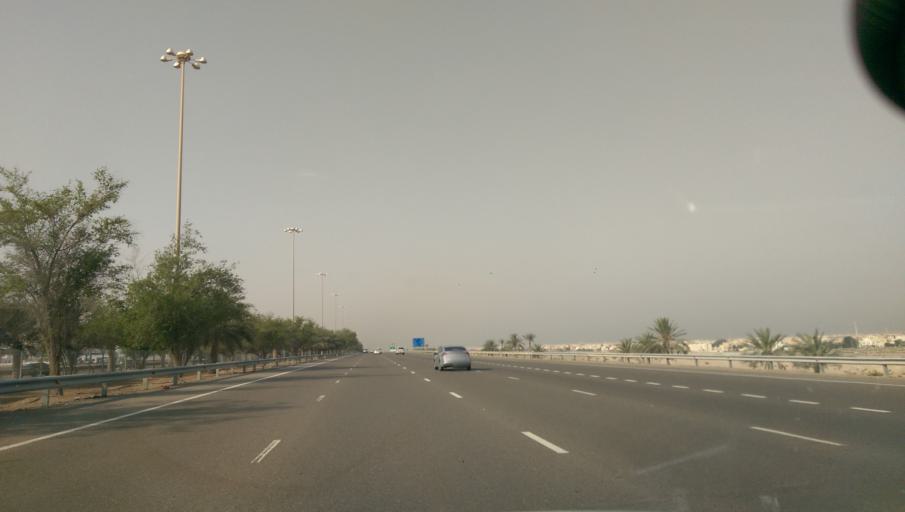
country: AE
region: Abu Dhabi
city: Abu Dhabi
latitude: 24.3912
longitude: 54.6645
